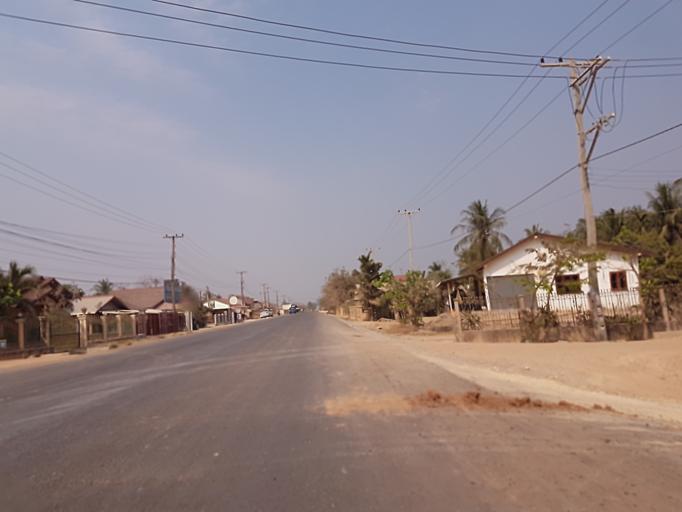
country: TH
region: Nong Khai
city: Nong Khai
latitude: 17.9213
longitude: 102.7681
